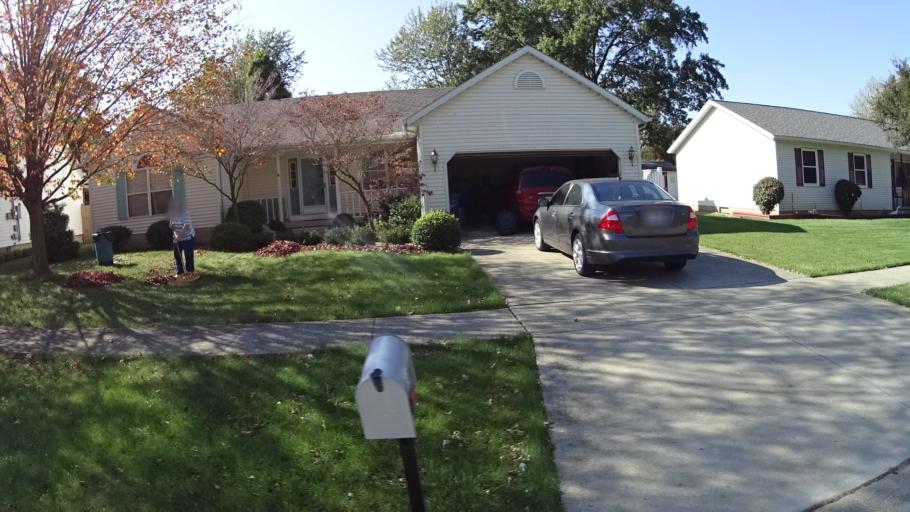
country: US
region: Ohio
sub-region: Lorain County
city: Vermilion
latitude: 41.4097
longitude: -82.3468
